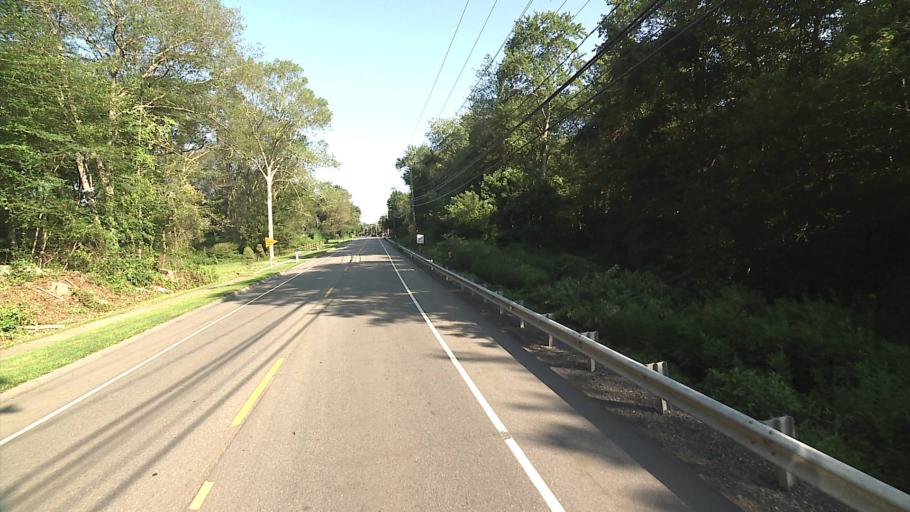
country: US
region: Connecticut
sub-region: New London County
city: Niantic
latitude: 41.3651
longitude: -72.1825
